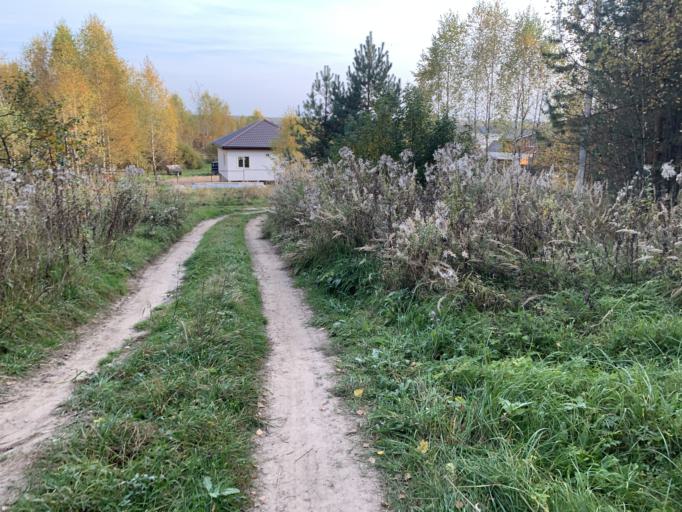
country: RU
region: Jaroslavl
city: Petrovsk
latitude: 56.9820
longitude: 39.3755
